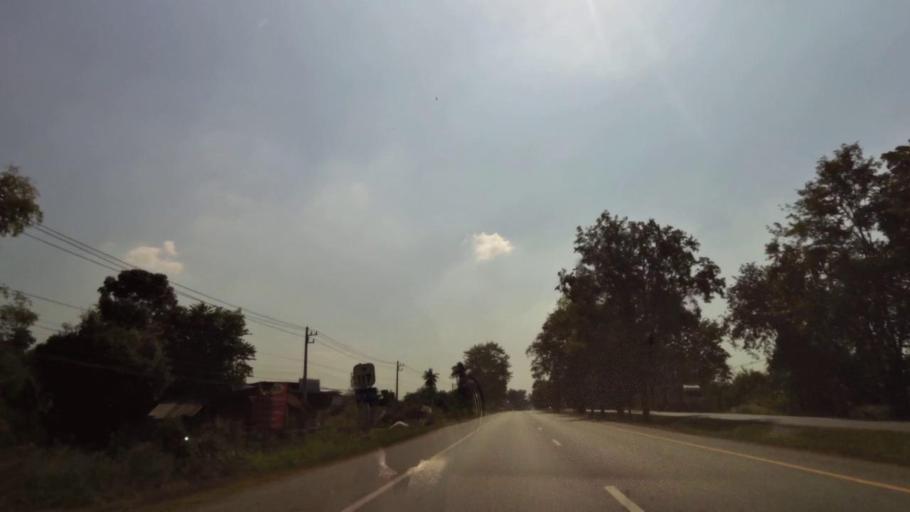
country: TH
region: Phichit
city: Bueng Na Rang
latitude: 16.1807
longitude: 100.1285
